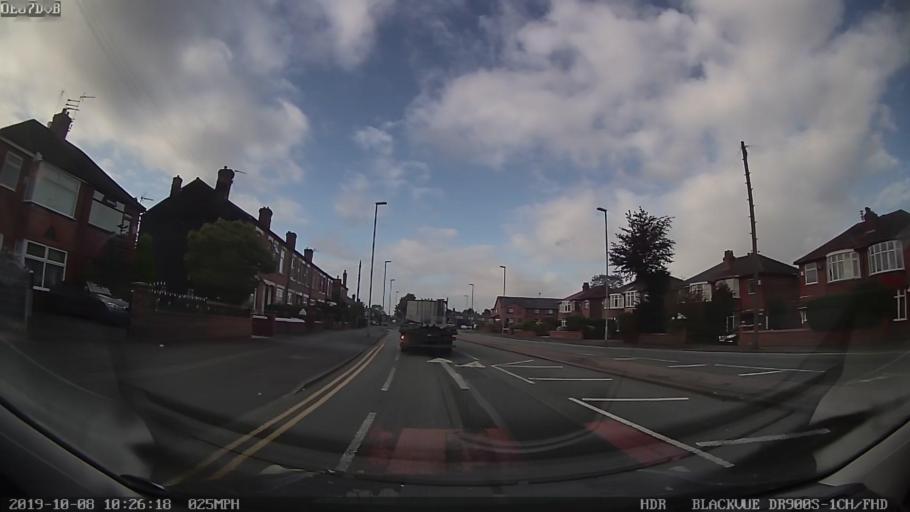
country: GB
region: England
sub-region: Manchester
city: Failsworth
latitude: 53.5223
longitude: -2.1591
